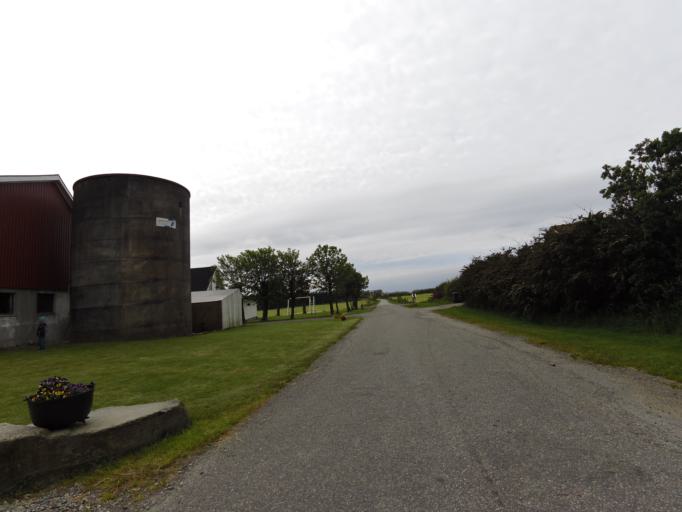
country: NO
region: Rogaland
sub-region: Ha
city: Naerbo
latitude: 58.6378
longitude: 5.6081
